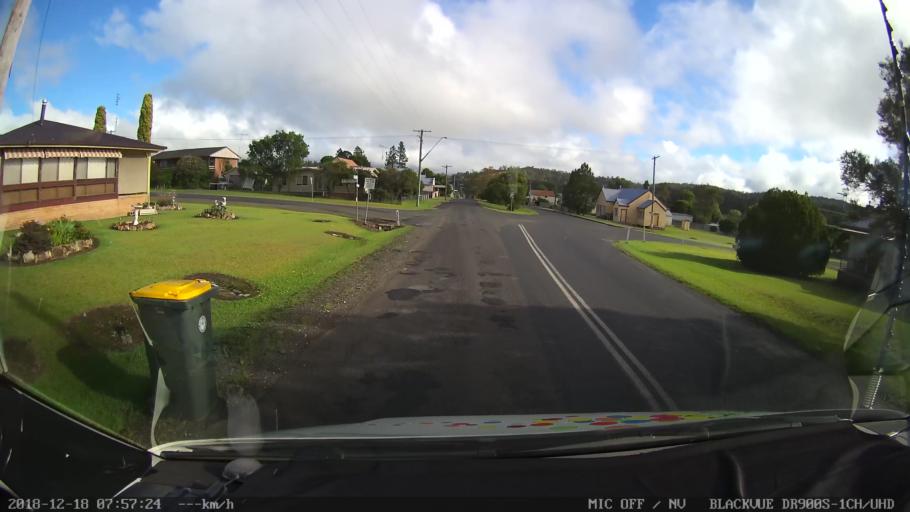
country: AU
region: New South Wales
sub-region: Kyogle
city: Kyogle
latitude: -28.3936
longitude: 152.6116
